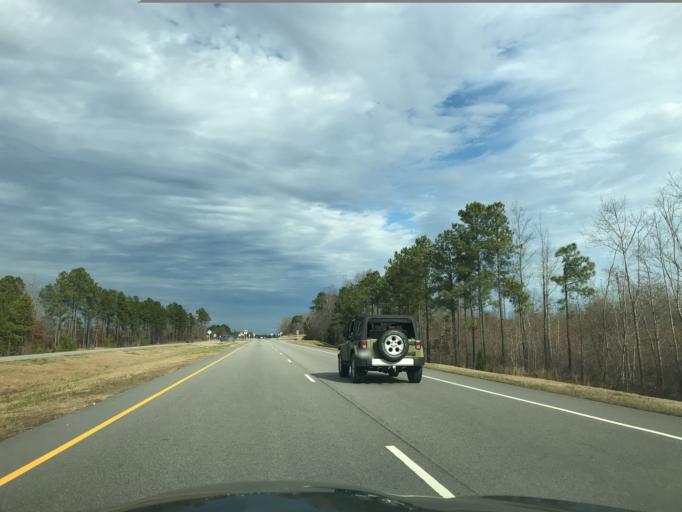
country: US
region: North Carolina
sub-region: Wake County
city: Rolesville
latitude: 35.9256
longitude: -78.4388
